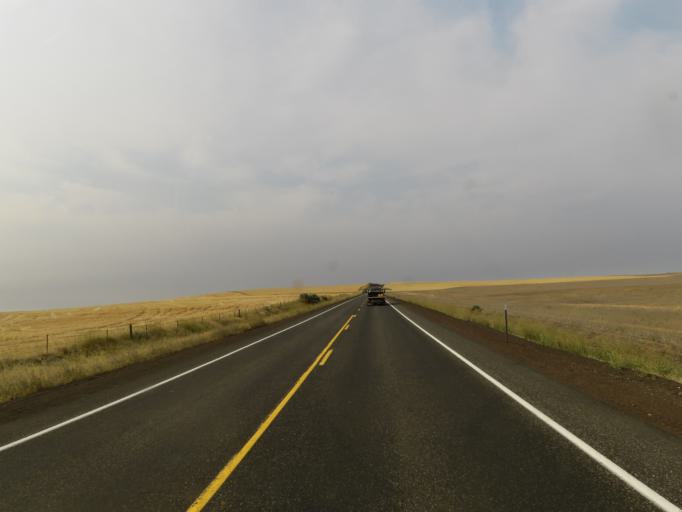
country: US
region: Oregon
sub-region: Sherman County
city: Moro
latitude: 45.4284
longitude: -120.7672
